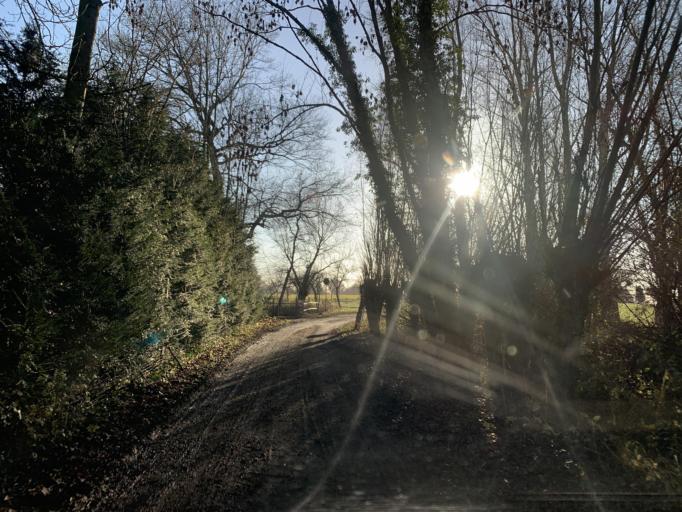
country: DE
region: North Rhine-Westphalia
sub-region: Regierungsbezirk Munster
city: Dulmen
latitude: 51.8761
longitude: 7.2737
